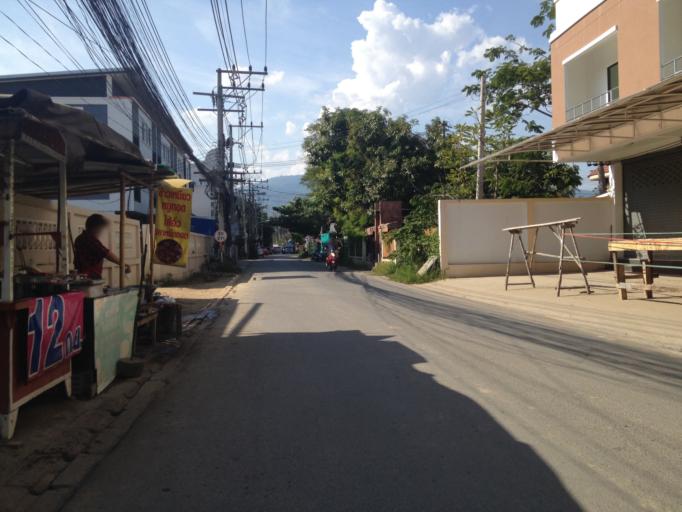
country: TH
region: Chiang Mai
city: Chiang Mai
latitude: 18.7627
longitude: 98.9795
